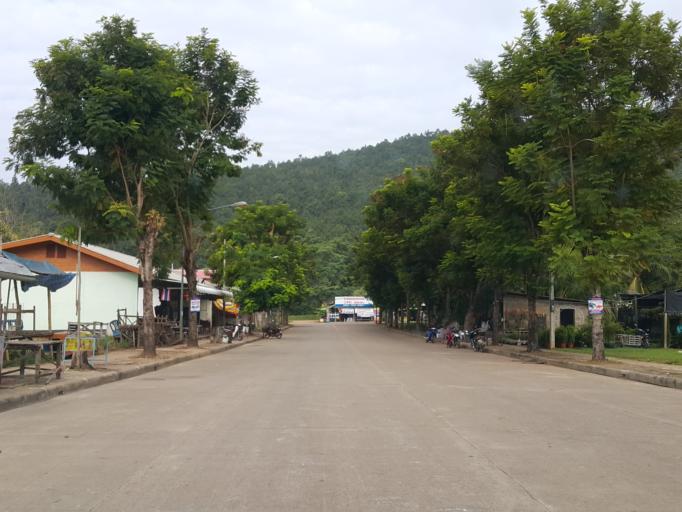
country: TH
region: Mae Hong Son
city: Mae Hong Son
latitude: 19.2930
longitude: 97.9630
